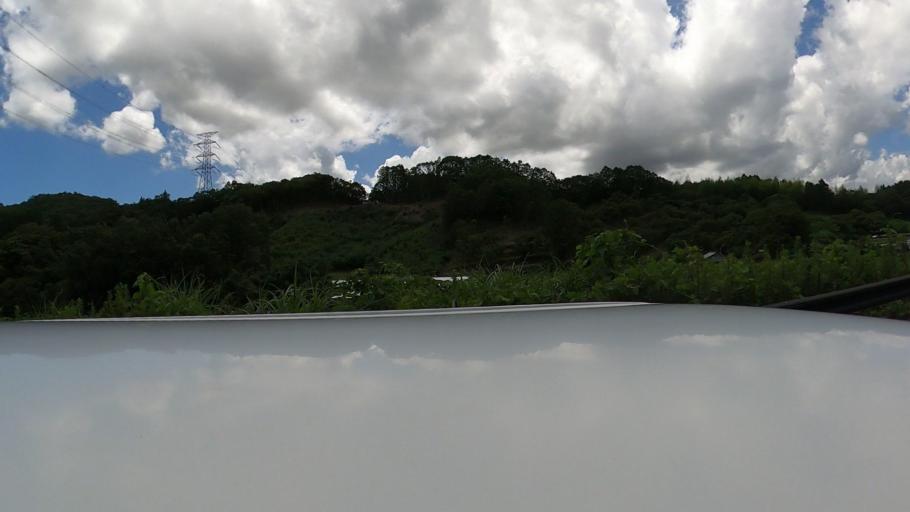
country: JP
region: Miyazaki
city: Nobeoka
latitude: 32.5811
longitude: 131.5187
